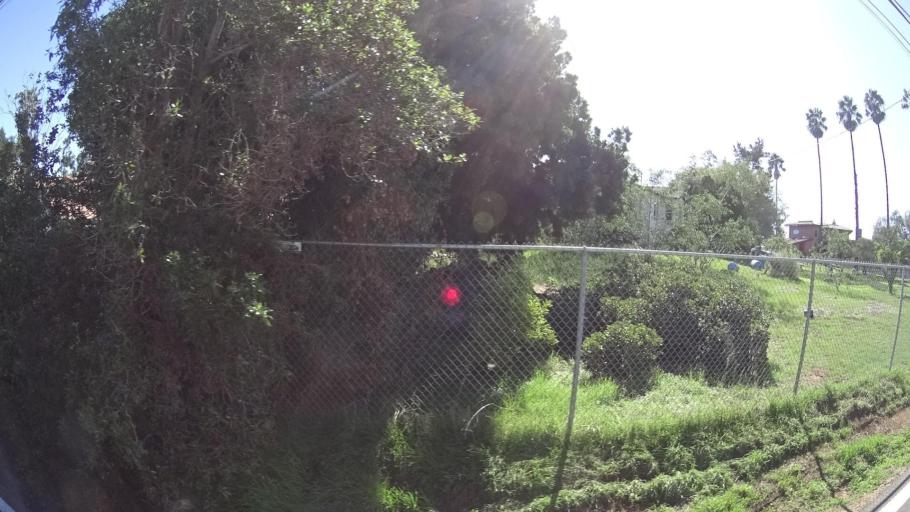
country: US
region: California
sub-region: San Diego County
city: Casa de Oro-Mount Helix
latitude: 32.7641
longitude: -116.9782
